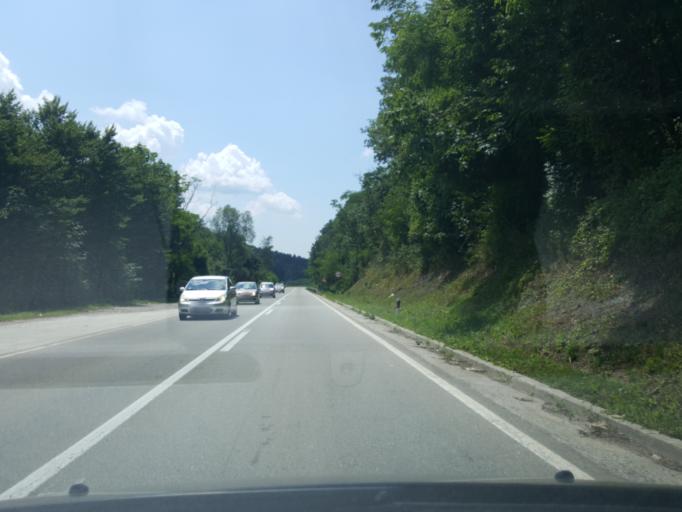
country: RS
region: Central Serbia
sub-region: Moravicki Okrug
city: Gornji Milanovac
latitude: 44.1098
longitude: 20.4833
